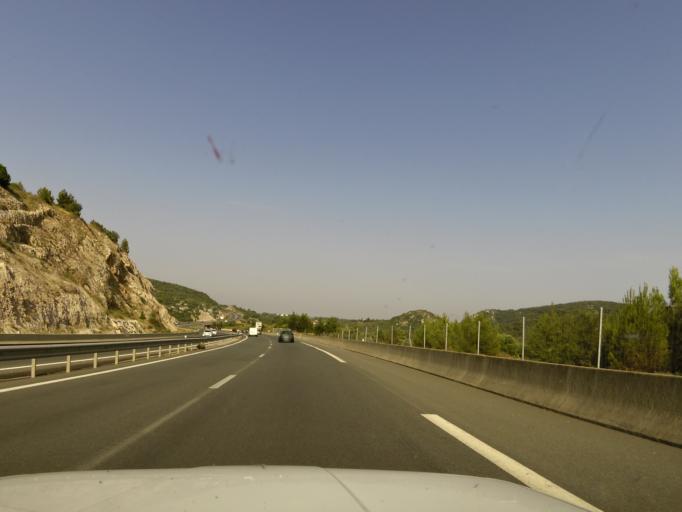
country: FR
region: Languedoc-Roussillon
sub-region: Departement de l'Herault
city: Montarnaud
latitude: 43.6255
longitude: 3.6520
